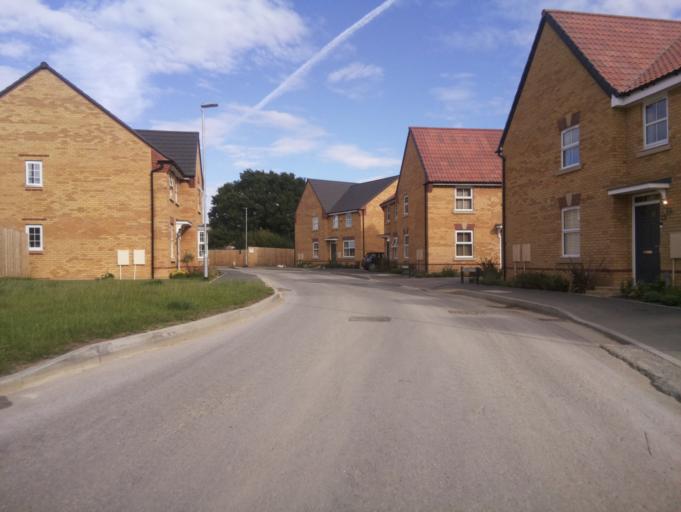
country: GB
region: England
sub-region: Gloucestershire
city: Stonehouse
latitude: 51.8055
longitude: -2.2686
